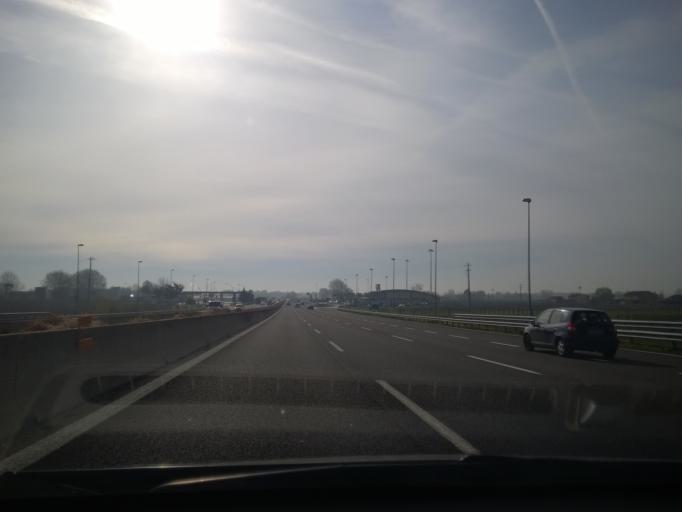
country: IT
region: Emilia-Romagna
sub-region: Provincia di Ravenna
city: Solarolo
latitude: 44.3439
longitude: 11.8441
